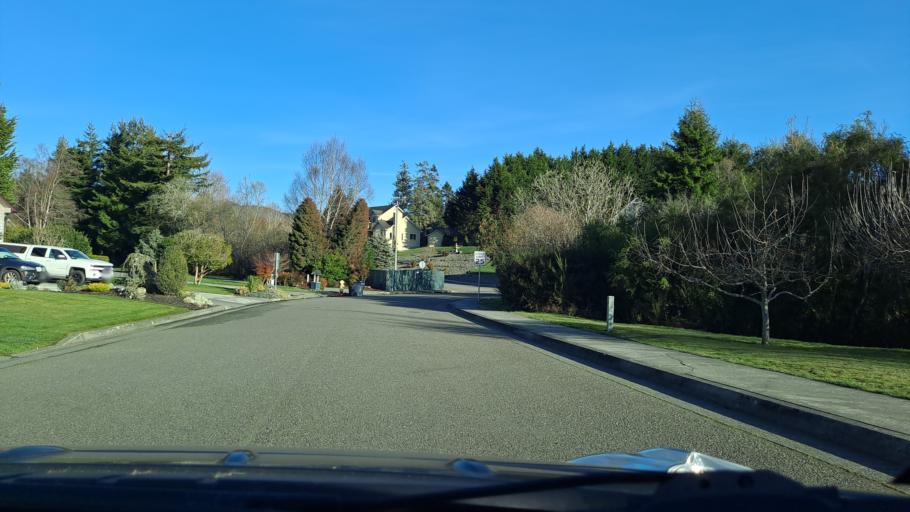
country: US
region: California
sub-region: Humboldt County
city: Fortuna
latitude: 40.5987
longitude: -124.1341
